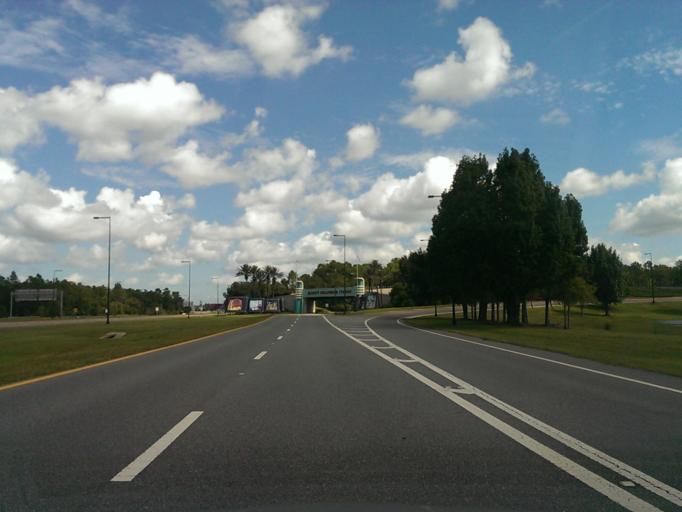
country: US
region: Florida
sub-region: Osceola County
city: Celebration
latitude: 28.3489
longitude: -81.5646
